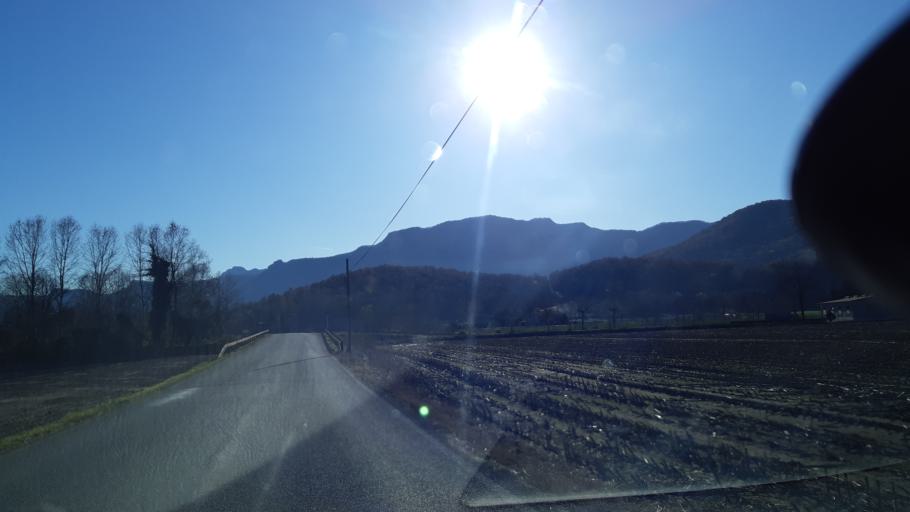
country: ES
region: Catalonia
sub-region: Provincia de Girona
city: Bas
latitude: 42.1446
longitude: 2.4408
